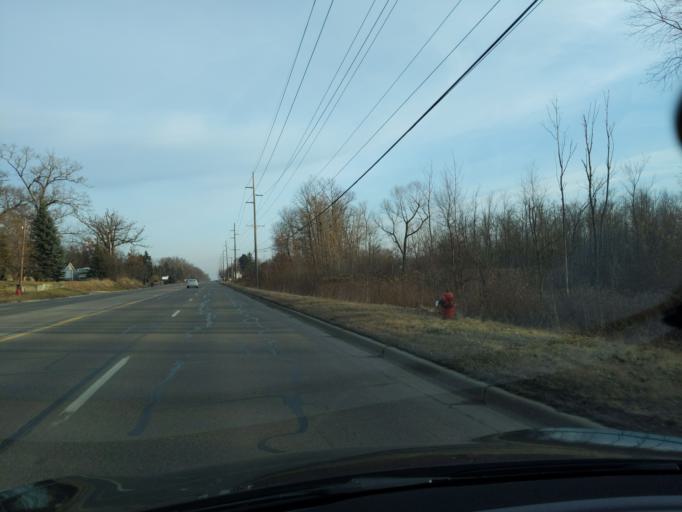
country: US
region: Michigan
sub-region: Livingston County
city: Brighton
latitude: 42.5782
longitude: -83.8490
